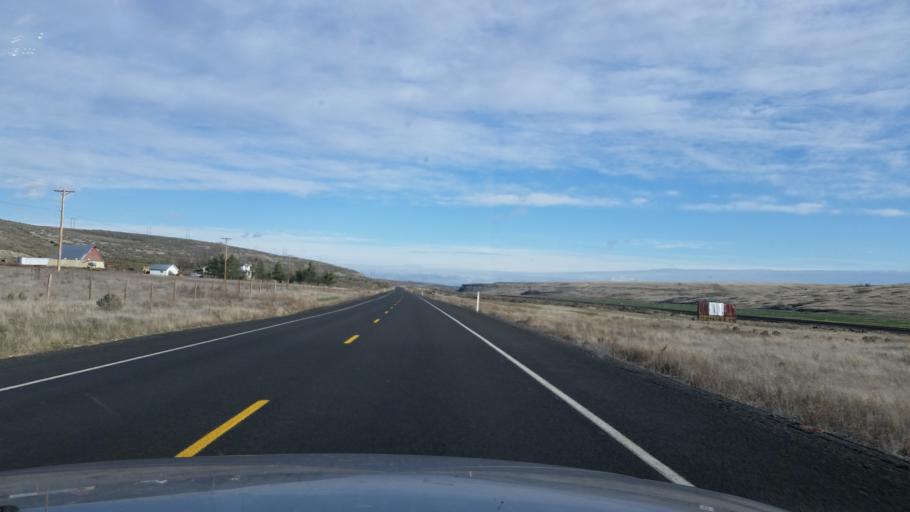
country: US
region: Washington
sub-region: Adams County
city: Ritzville
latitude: 47.3488
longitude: -118.5519
